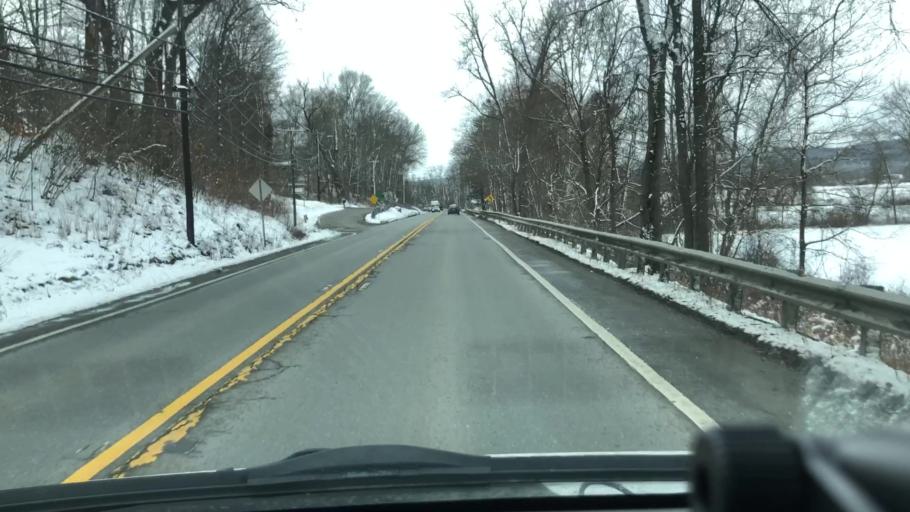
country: US
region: Massachusetts
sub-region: Franklin County
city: Greenfield
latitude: 42.5610
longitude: -72.5948
